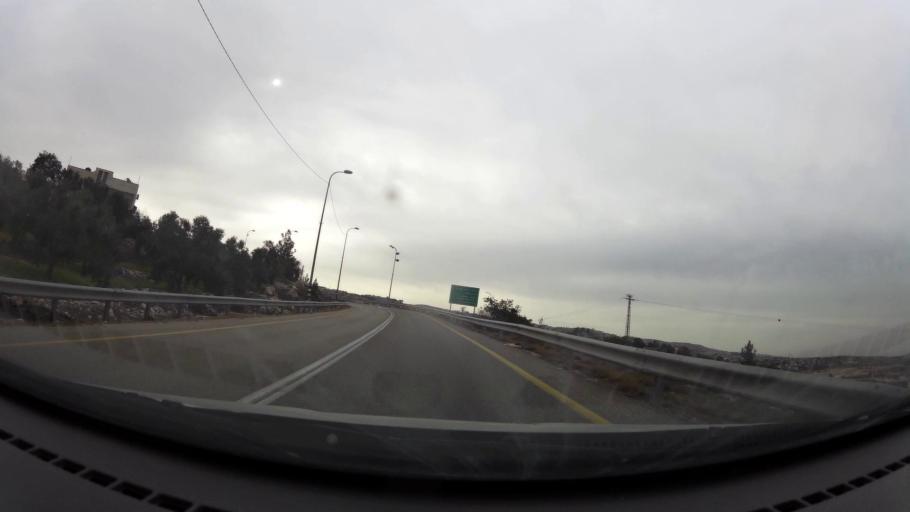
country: PS
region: West Bank
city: Surif
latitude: 31.6701
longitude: 35.0734
